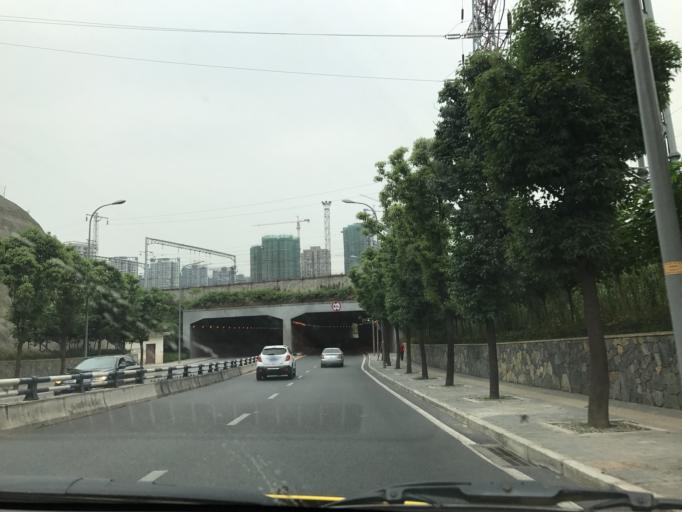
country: CN
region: Chongqing Shi
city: Cuntan
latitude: 29.6132
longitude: 106.5547
